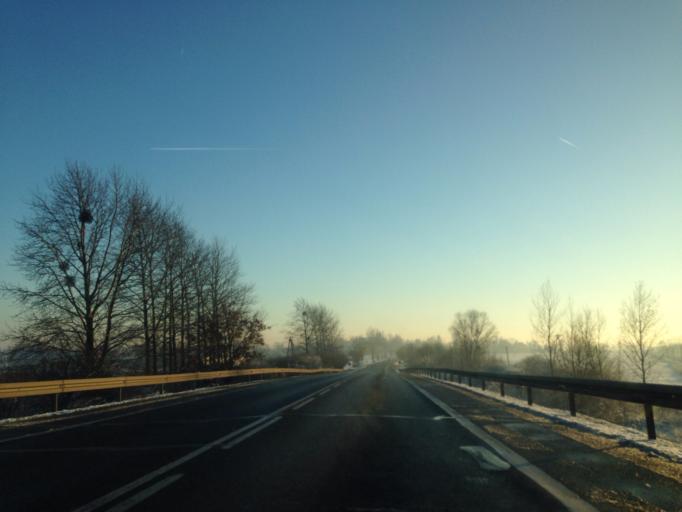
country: PL
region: Pomeranian Voivodeship
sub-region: Powiat tczewski
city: Subkowy
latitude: 54.0114
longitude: 18.7650
